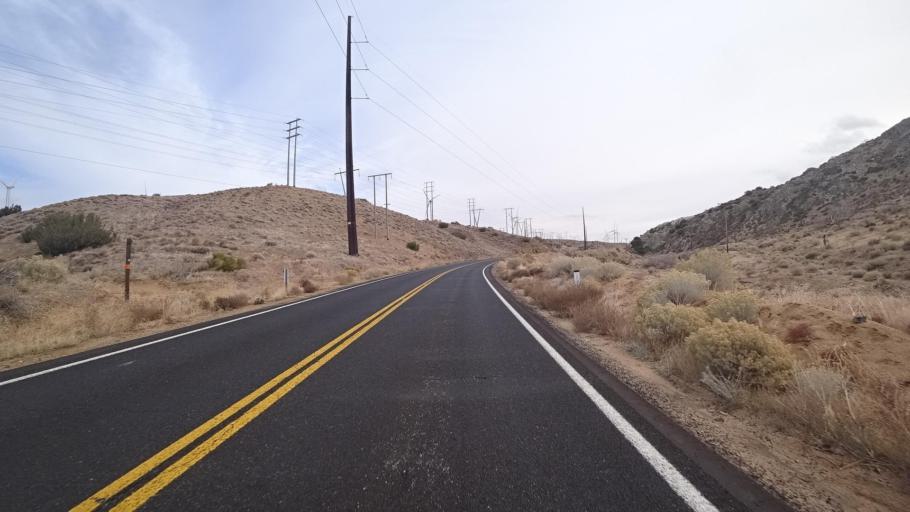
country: US
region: California
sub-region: Kern County
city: Tehachapi
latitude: 35.0523
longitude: -118.3412
